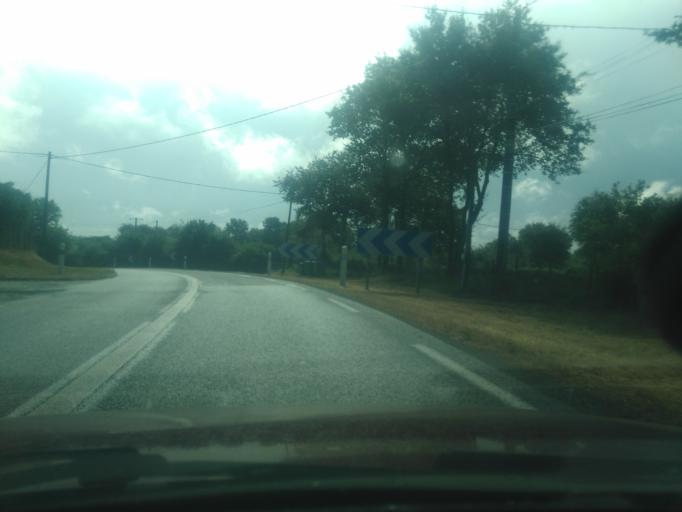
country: FR
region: Poitou-Charentes
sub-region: Departement des Deux-Sevres
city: Le Tallud
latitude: 46.6252
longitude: -0.3188
